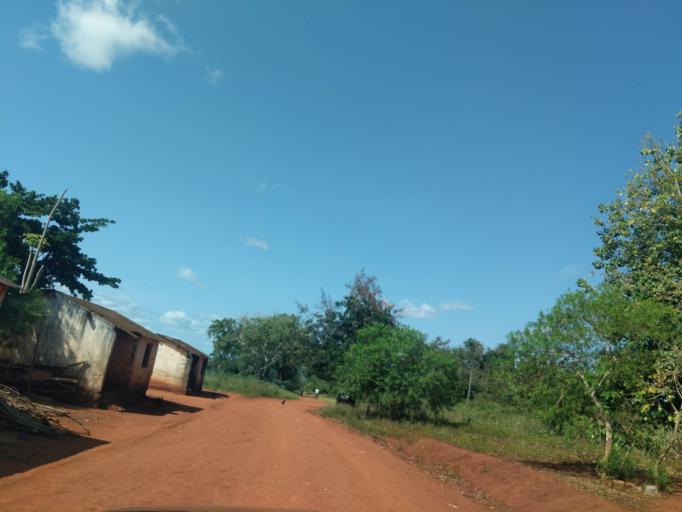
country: TZ
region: Tanga
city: Muheza
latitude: -5.3892
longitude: 38.5755
